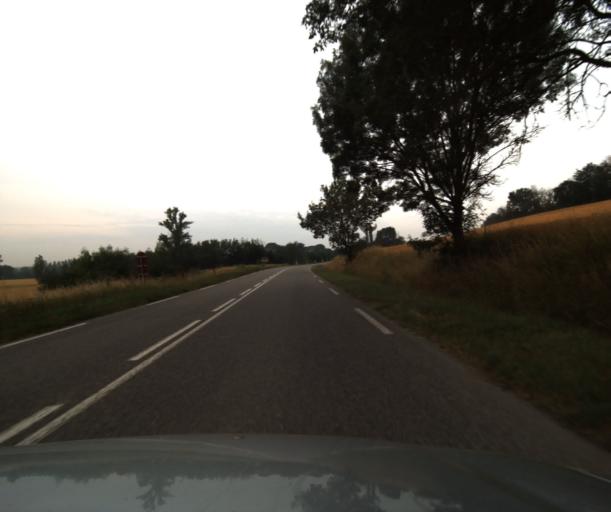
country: FR
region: Midi-Pyrenees
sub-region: Departement du Tarn-et-Garonne
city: Beaumont-de-Lomagne
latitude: 43.8682
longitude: 0.9613
